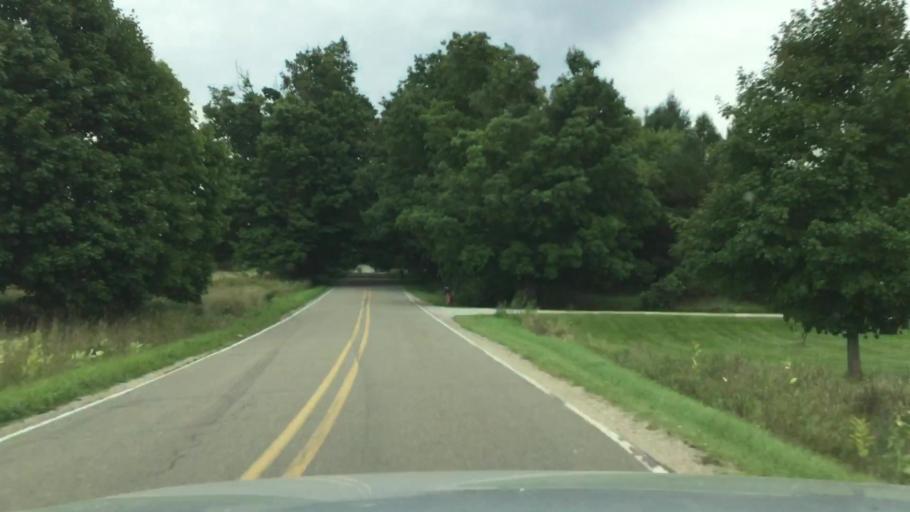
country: US
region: Michigan
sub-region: Shiawassee County
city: Durand
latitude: 42.8296
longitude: -84.0289
